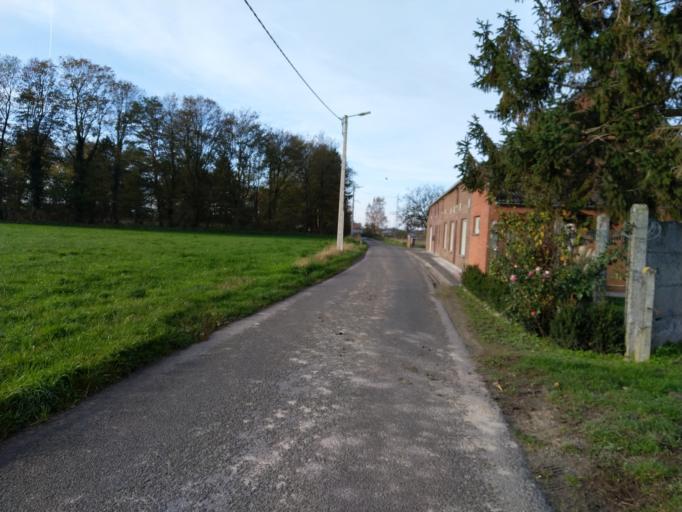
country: BE
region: Wallonia
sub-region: Province du Hainaut
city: Saint-Ghislain
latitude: 50.5089
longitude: 3.8083
